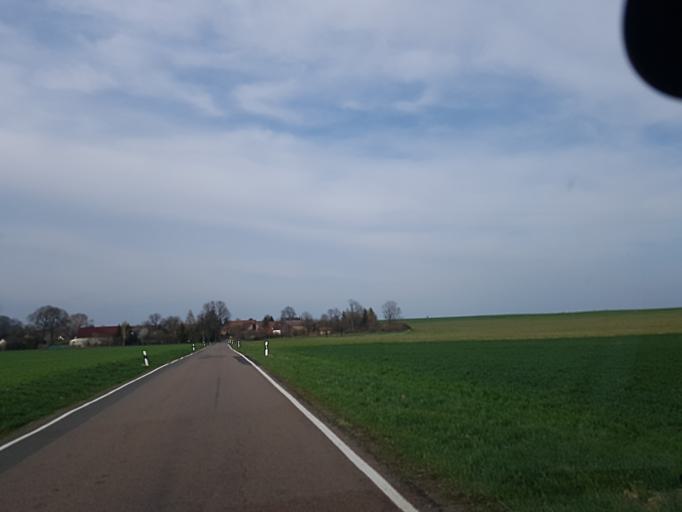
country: DE
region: Saxony
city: Strehla
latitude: 51.3634
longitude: 13.1922
